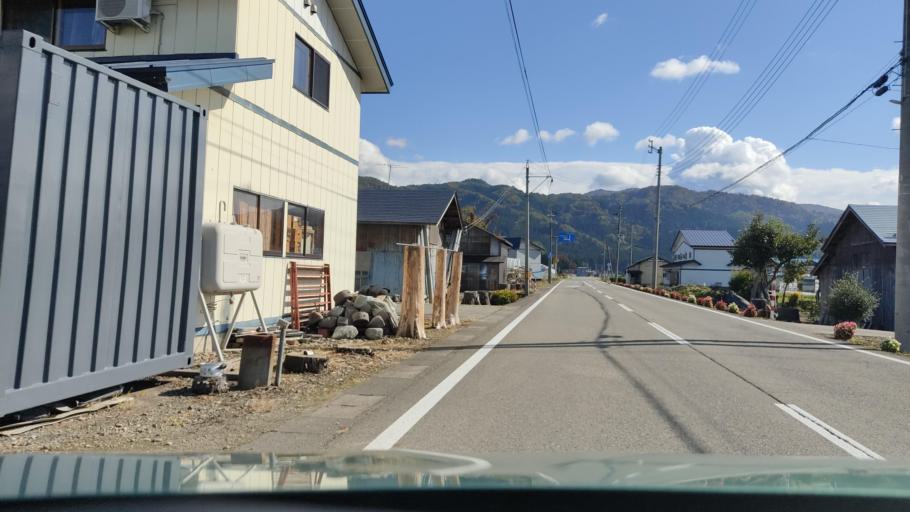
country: JP
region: Akita
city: Yokotemachi
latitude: 39.4067
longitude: 140.5762
